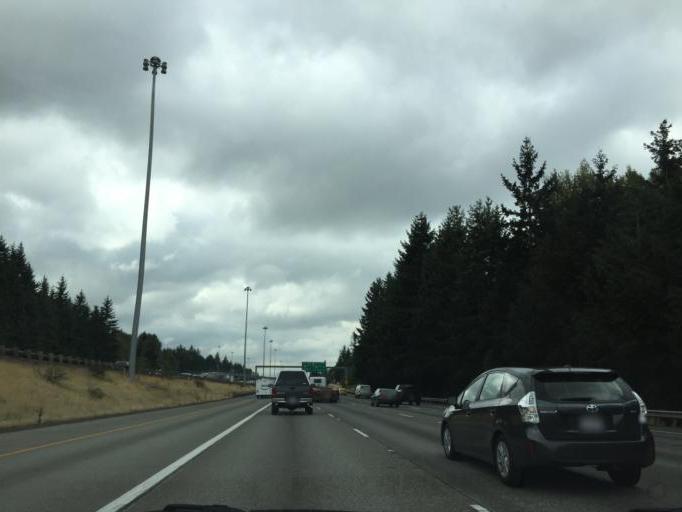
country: US
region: Washington
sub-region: King County
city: Federal Way
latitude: 47.2962
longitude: -122.3046
